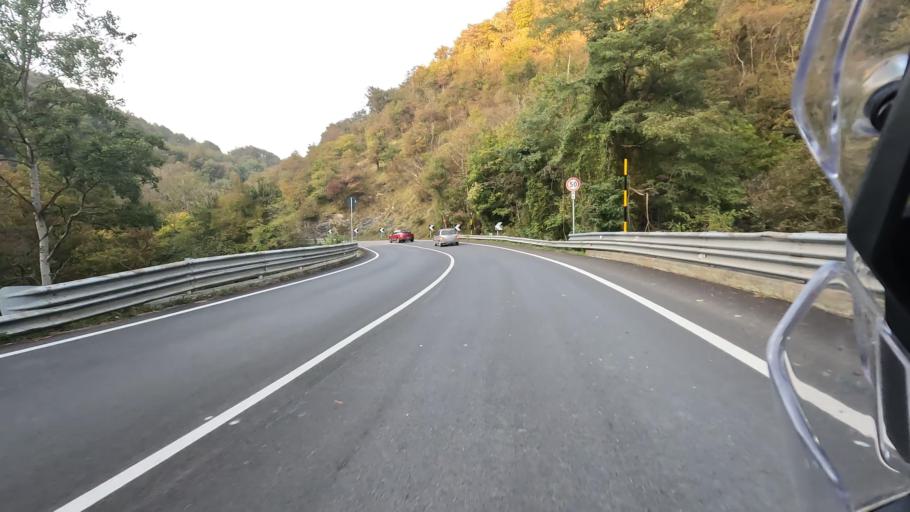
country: IT
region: Liguria
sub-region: Provincia di Savona
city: Osteria dei Cacciatori-Stella
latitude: 44.4512
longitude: 8.4786
